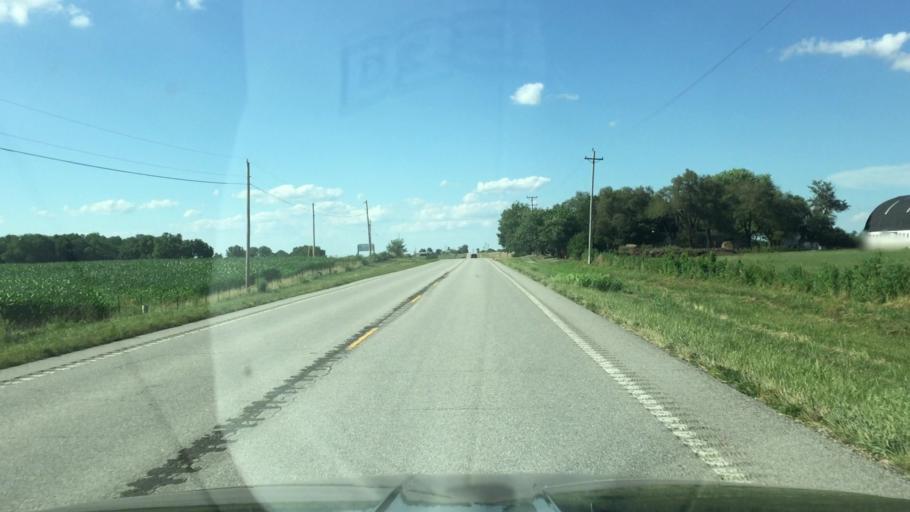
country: US
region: Missouri
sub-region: Morgan County
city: Versailles
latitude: 38.4844
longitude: -92.8085
